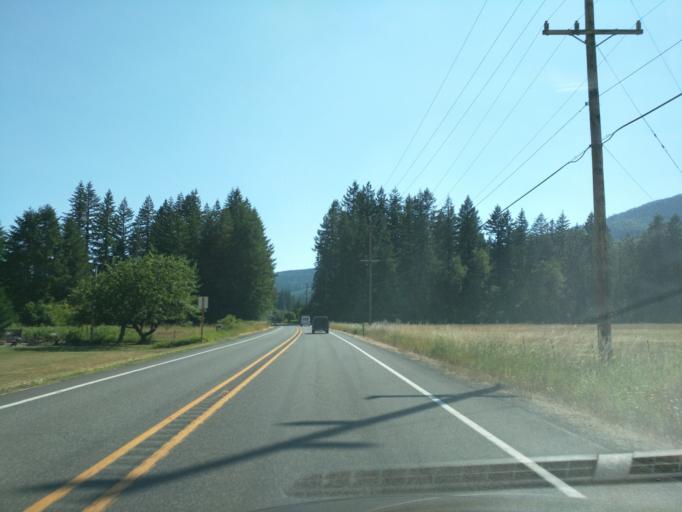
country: US
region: Washington
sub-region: Whatcom County
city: Peaceful Valley
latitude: 48.8983
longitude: -122.1459
